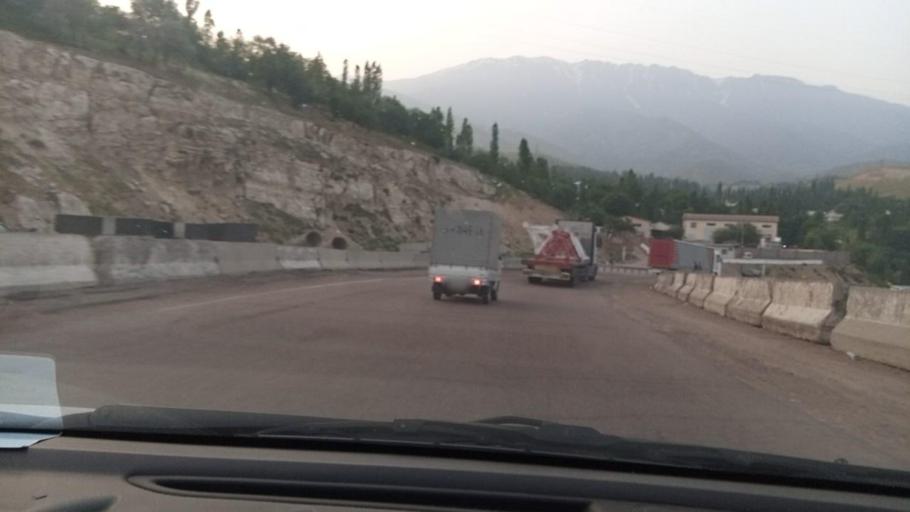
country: UZ
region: Toshkent
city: Angren
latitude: 41.0733
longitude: 70.2517
